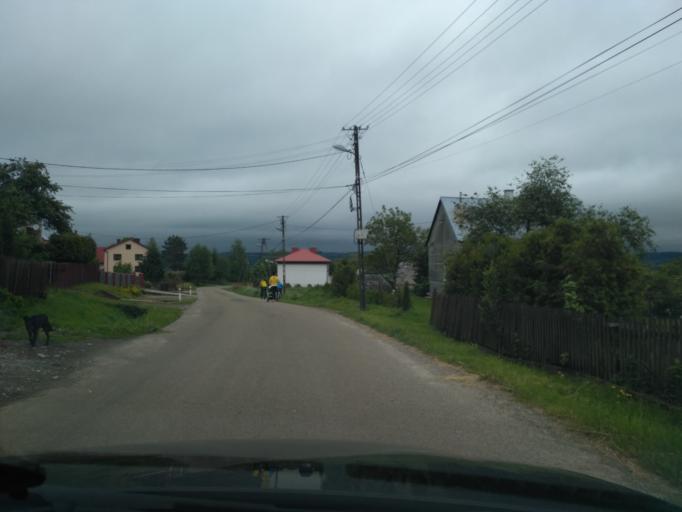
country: PL
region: Subcarpathian Voivodeship
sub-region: Powiat jasielski
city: Brzyska
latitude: 49.8235
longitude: 21.3673
